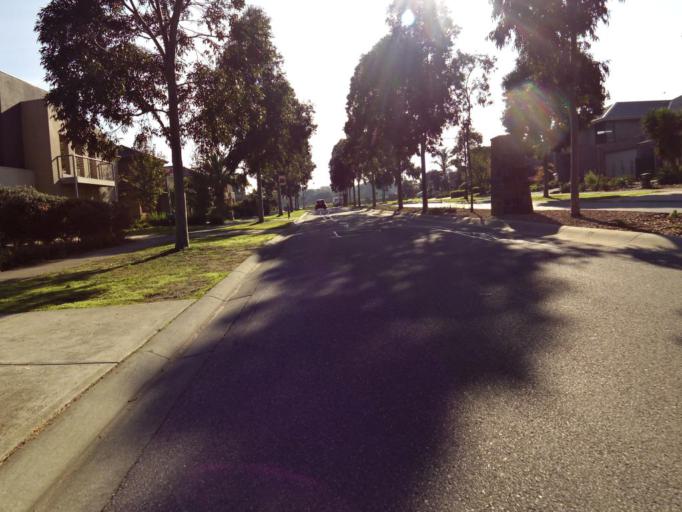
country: AU
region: Victoria
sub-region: Kingston
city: Waterways
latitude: -38.0120
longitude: 145.1321
